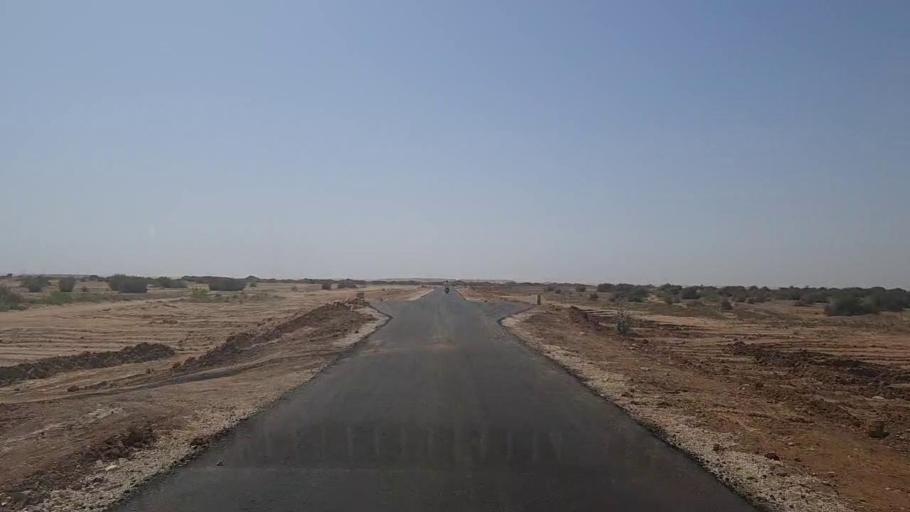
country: PK
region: Sindh
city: Kotri
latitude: 25.1468
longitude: 68.2022
